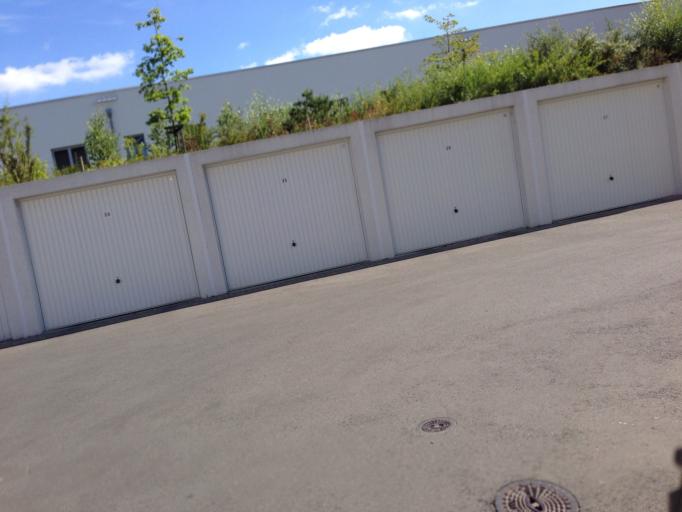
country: DE
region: Hesse
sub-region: Regierungsbezirk Darmstadt
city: Grosskrotzenburg
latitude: 50.1179
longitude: 8.9594
